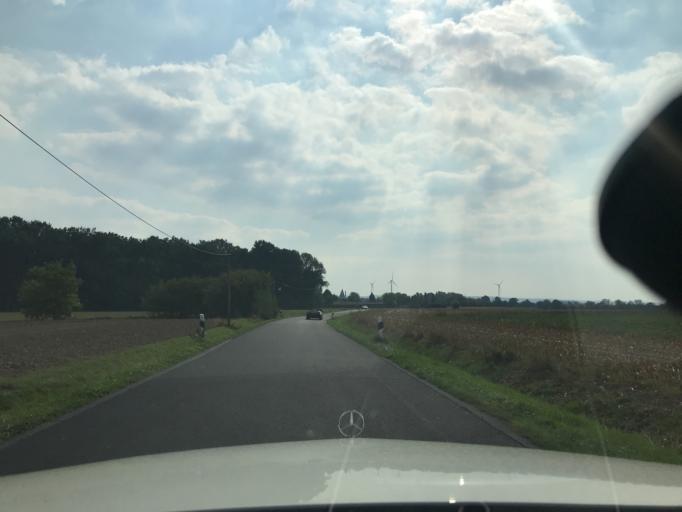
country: DE
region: North Rhine-Westphalia
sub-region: Regierungsbezirk Arnsberg
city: Werl
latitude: 51.5867
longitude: 7.8697
